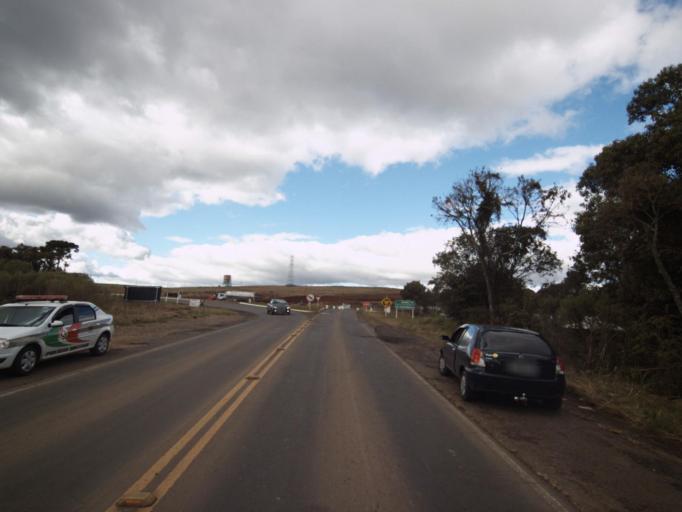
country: BR
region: Santa Catarina
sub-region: Joacaba
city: Joacaba
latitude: -27.0977
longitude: -51.6537
